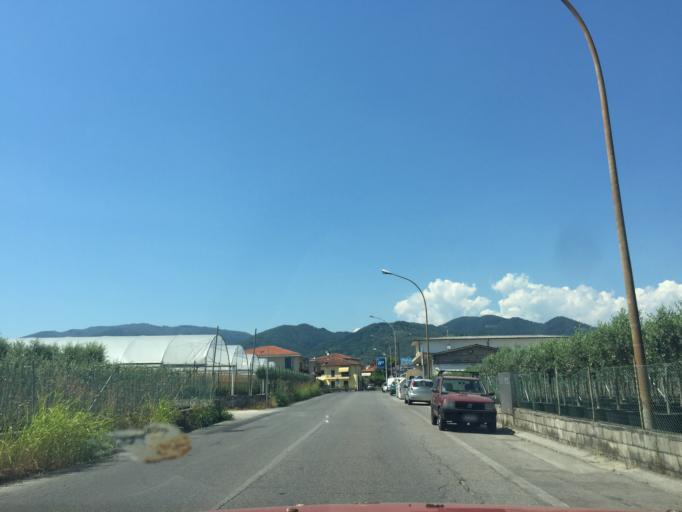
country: IT
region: Tuscany
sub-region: Provincia di Pistoia
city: Pescia
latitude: 43.8771
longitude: 10.6896
